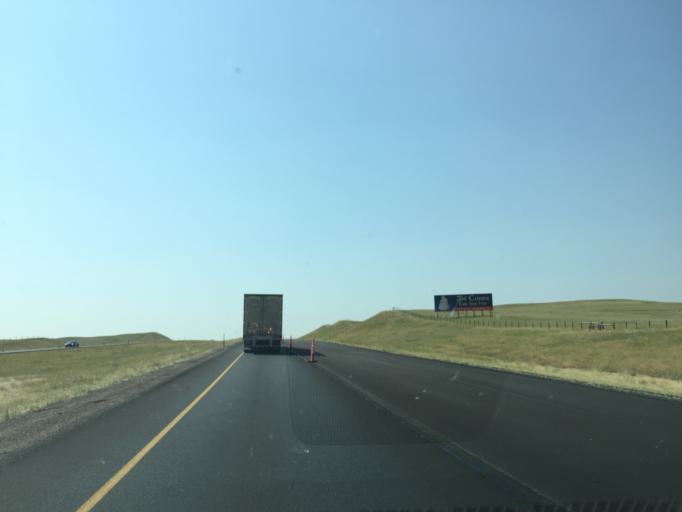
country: US
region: Wyoming
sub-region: Laramie County
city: Ranchettes
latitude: 41.3216
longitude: -104.8613
